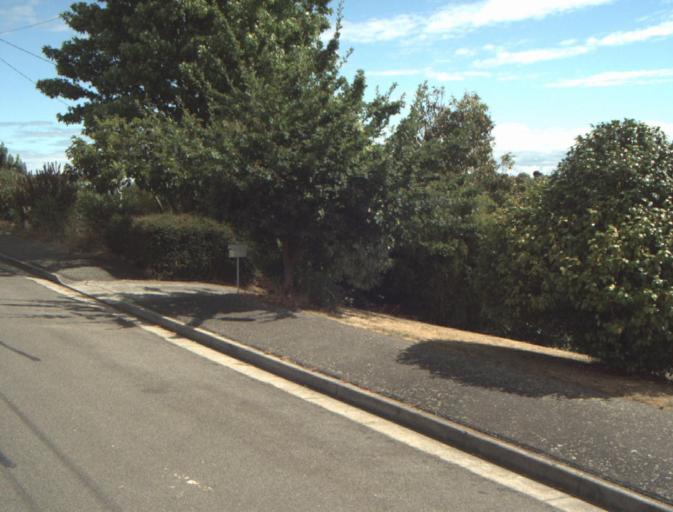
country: AU
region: Tasmania
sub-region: Launceston
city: West Launceston
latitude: -41.4556
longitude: 147.1281
